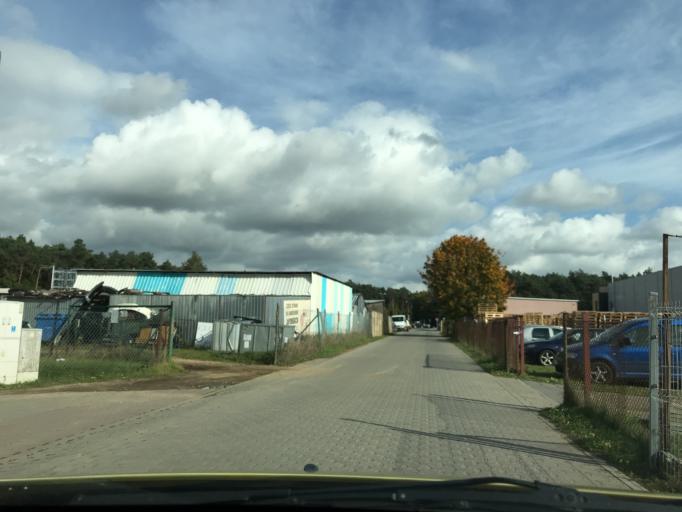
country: PL
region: Greater Poland Voivodeship
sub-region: Powiat poznanski
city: Baranowo
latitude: 52.4139
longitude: 16.7877
